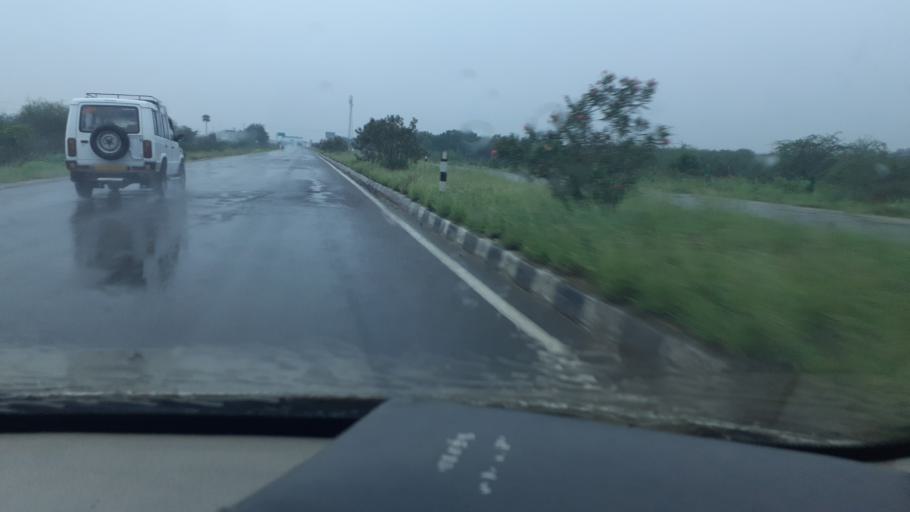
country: IN
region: Tamil Nadu
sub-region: Virudhunagar
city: Sattur
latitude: 9.3984
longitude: 77.9162
